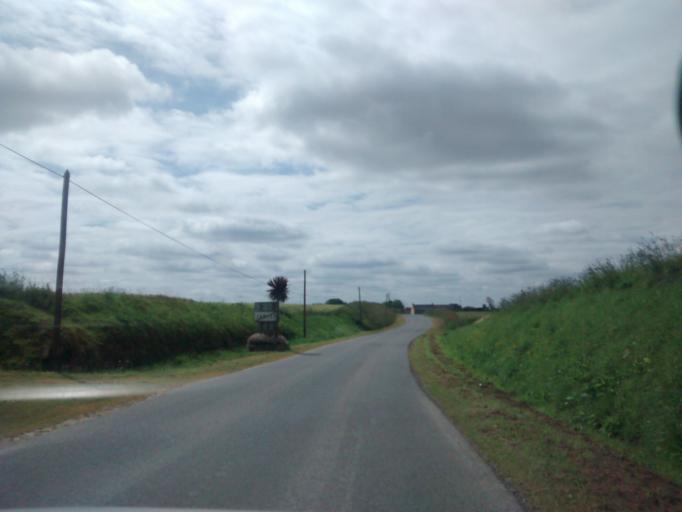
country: FR
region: Brittany
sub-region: Departement des Cotes-d'Armor
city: Langoat
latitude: 48.7744
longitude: -3.3038
